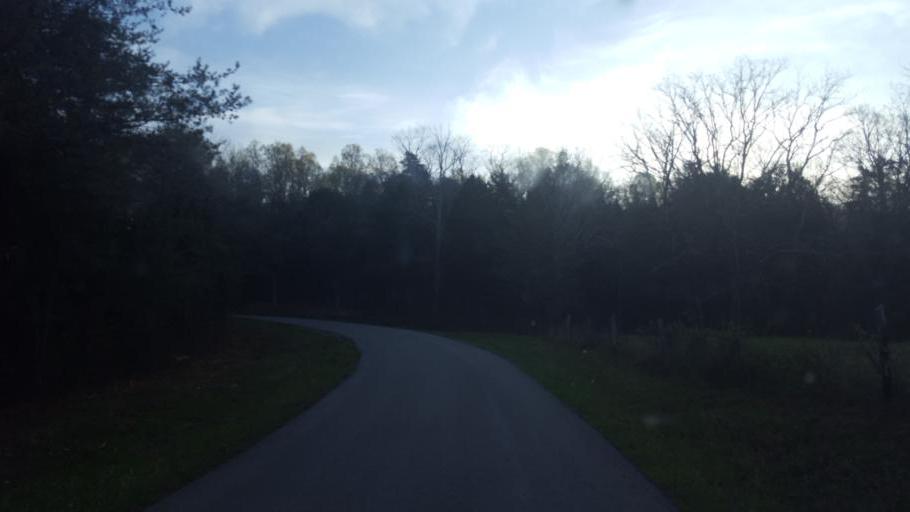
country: US
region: Kentucky
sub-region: Barren County
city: Cave City
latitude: 37.2062
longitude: -86.0162
